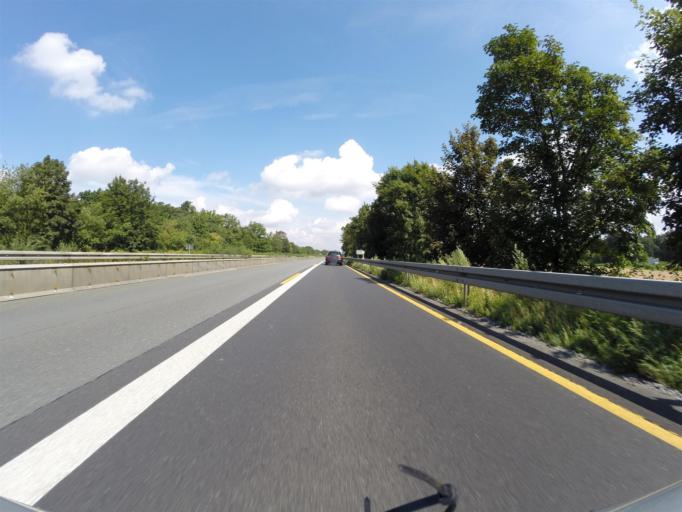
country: DE
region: North Rhine-Westphalia
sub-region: Regierungsbezirk Detmold
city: Hovelhof
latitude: 51.8084
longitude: 8.6987
